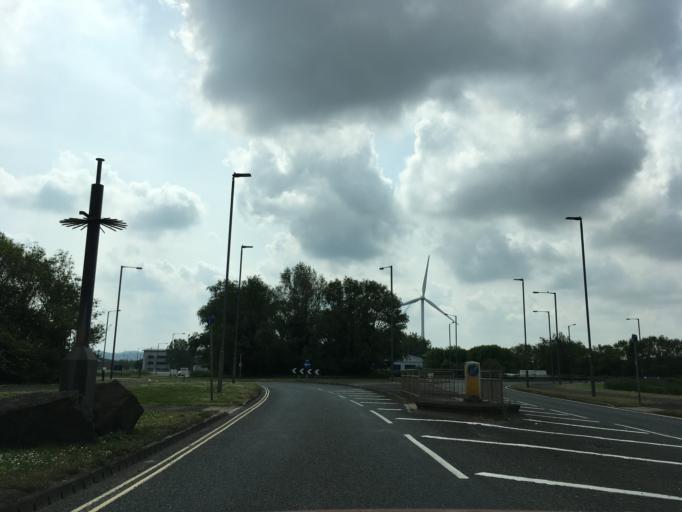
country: GB
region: England
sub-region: South Gloucestershire
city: Severn Beach
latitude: 51.5198
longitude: -2.6764
